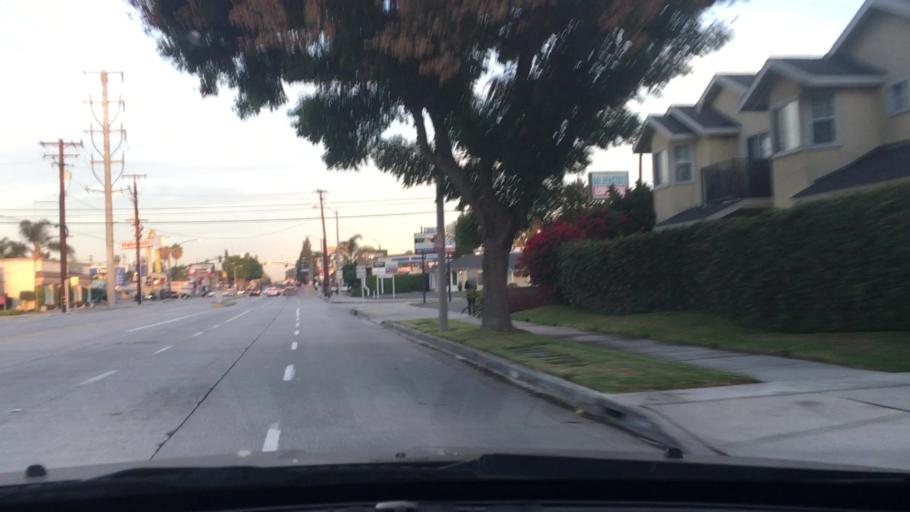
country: US
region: California
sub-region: Los Angeles County
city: Downey
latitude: 33.9467
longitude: -118.1154
